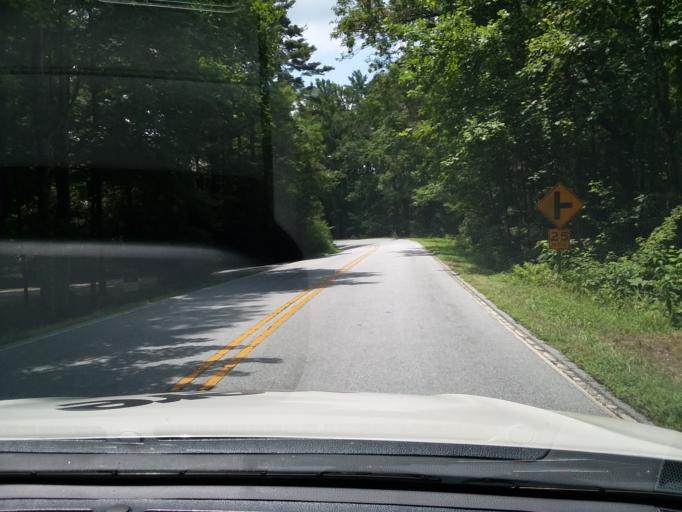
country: US
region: Georgia
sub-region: Rabun County
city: Mountain City
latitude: 35.0296
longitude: -83.1930
